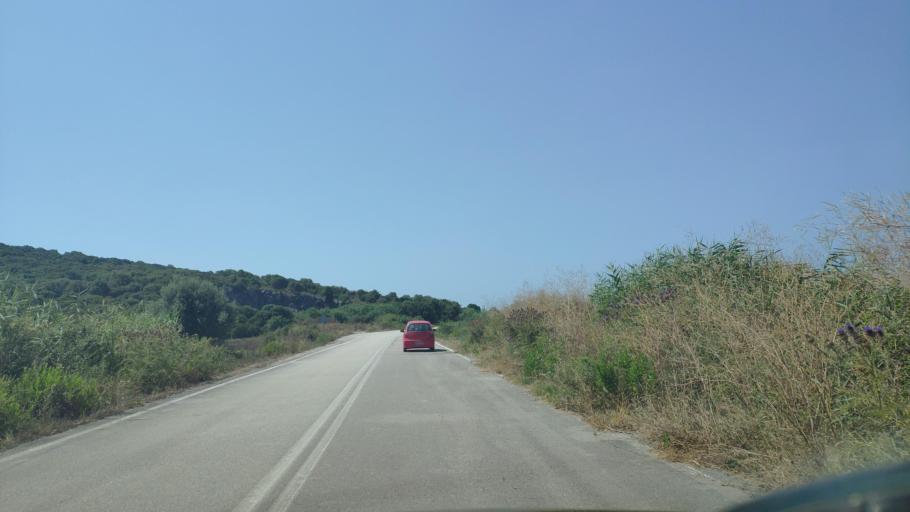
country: GR
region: Epirus
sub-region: Nomos Artas
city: Aneza
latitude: 39.0429
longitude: 20.8600
